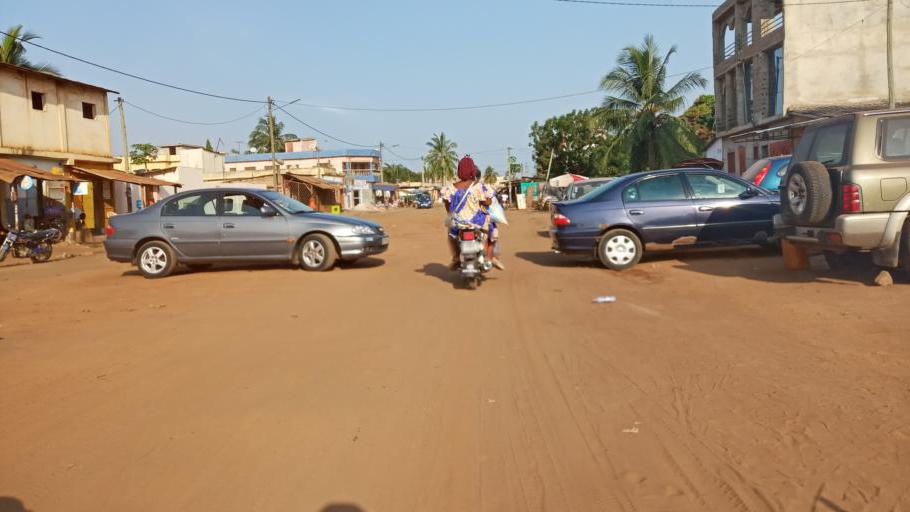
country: TG
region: Maritime
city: Lome
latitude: 6.1810
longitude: 1.1652
